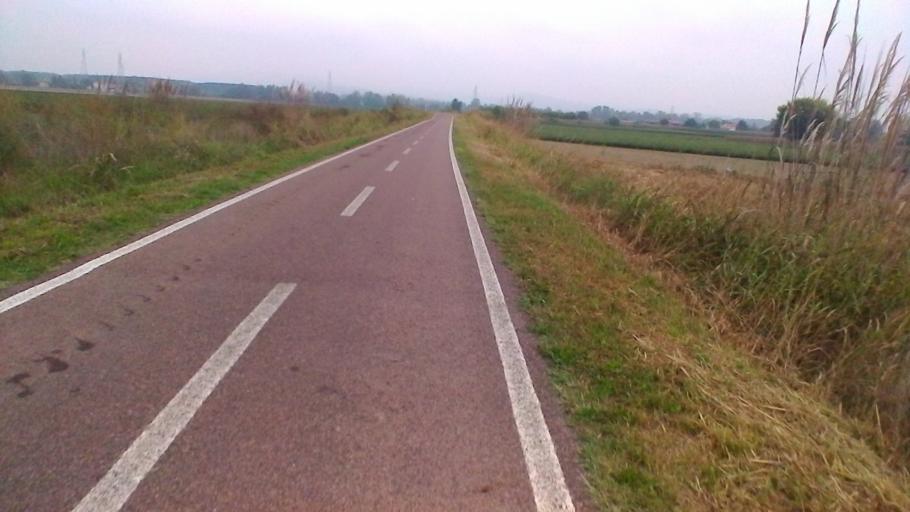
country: IT
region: Veneto
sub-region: Provincia di Verona
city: Campagnola
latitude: 45.3867
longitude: 11.0712
